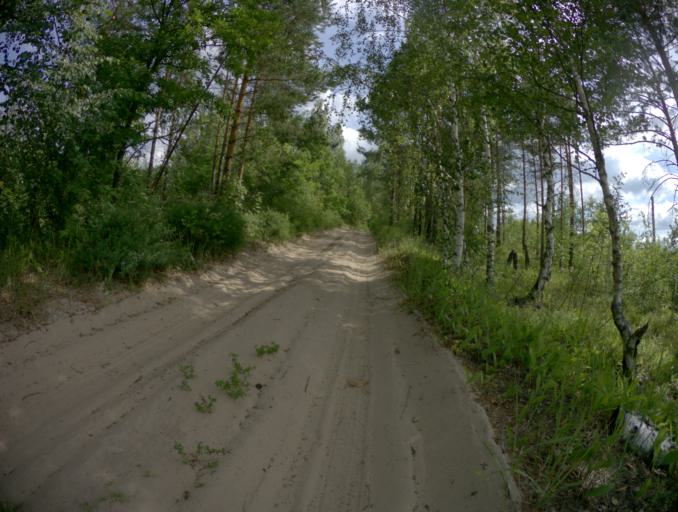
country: RU
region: Ivanovo
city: Talitsy
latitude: 56.5361
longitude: 42.4443
